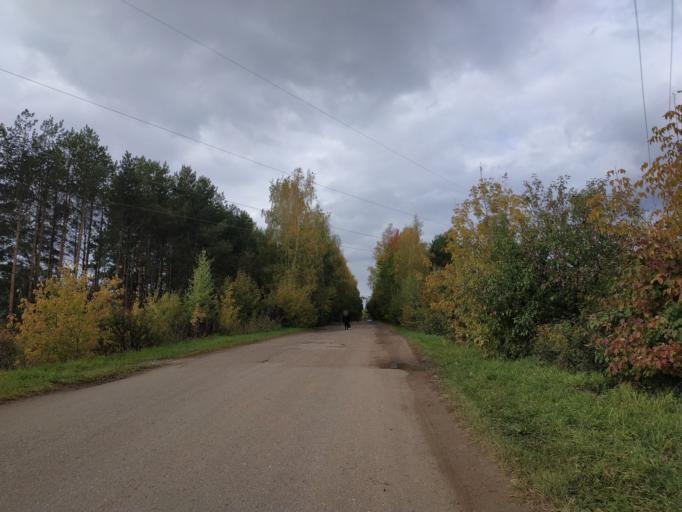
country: RU
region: Chuvashia
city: Ishley
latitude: 56.1279
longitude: 47.0910
